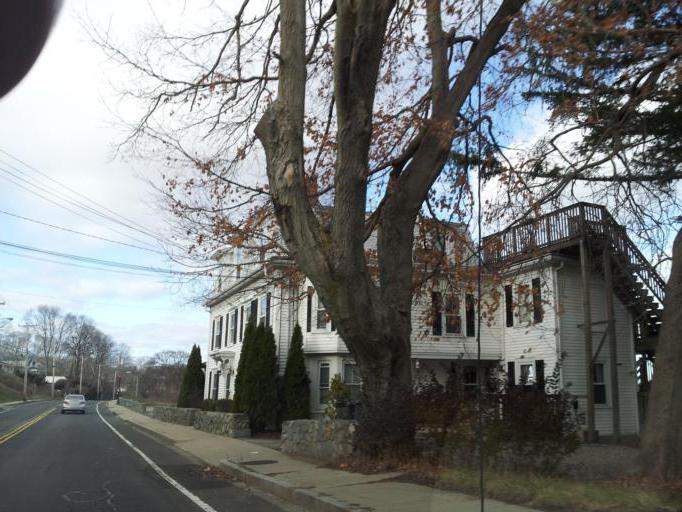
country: US
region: Massachusetts
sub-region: Plymouth County
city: Plymouth
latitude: 41.9485
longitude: -70.6492
